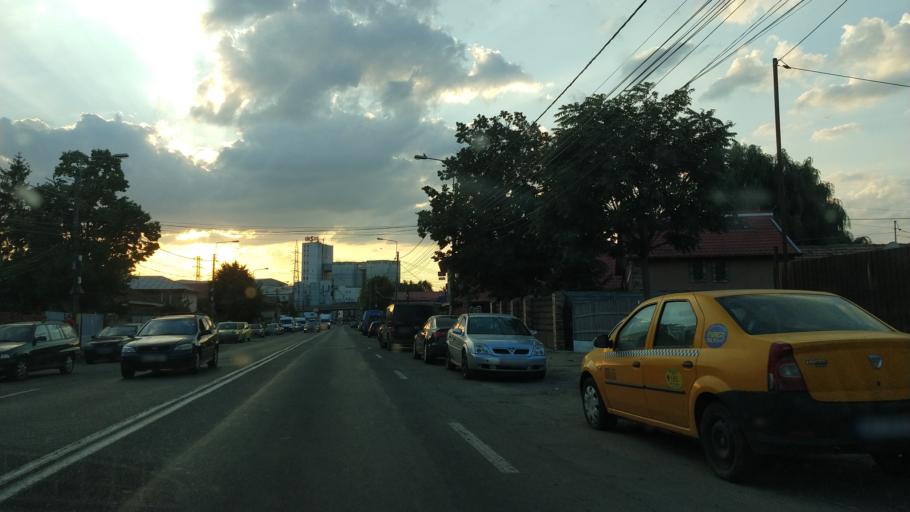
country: RO
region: Buzau
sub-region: Comuna Maracineni
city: Potoceni
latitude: 45.1621
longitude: 26.7922
